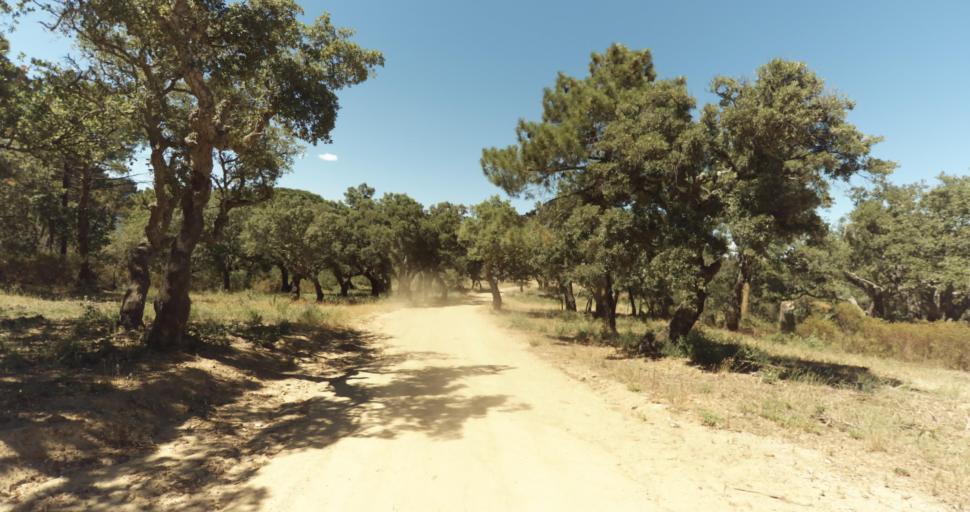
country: FR
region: Provence-Alpes-Cote d'Azur
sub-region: Departement du Var
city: Gassin
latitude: 43.2521
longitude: 6.5645
